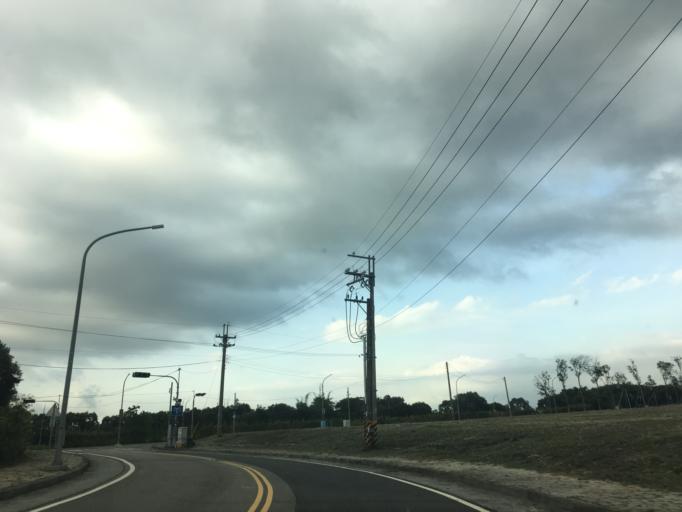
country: TW
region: Taiwan
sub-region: Taichung City
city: Taichung
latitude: 24.1747
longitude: 120.7683
